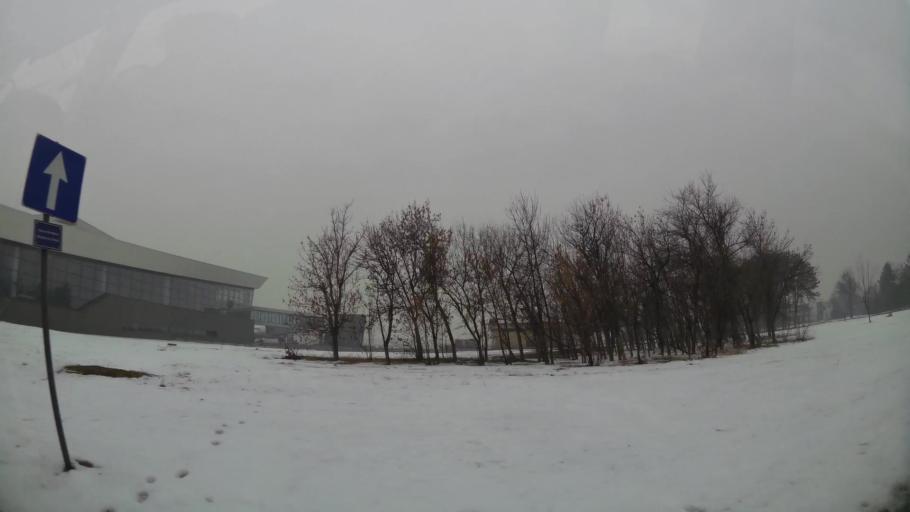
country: MK
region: Petrovec
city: Petrovec
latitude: 41.9623
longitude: 21.6273
